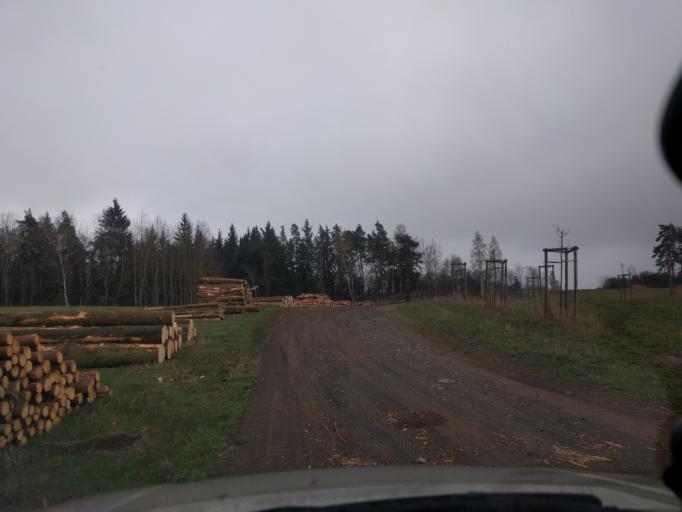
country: CZ
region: Karlovarsky
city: Bochov
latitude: 50.1078
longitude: 13.0930
